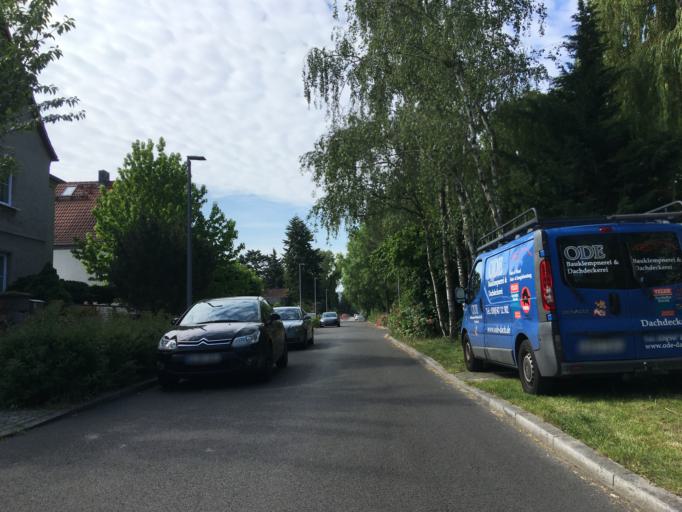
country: DE
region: Berlin
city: Biesdorf
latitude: 52.5188
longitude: 13.5334
